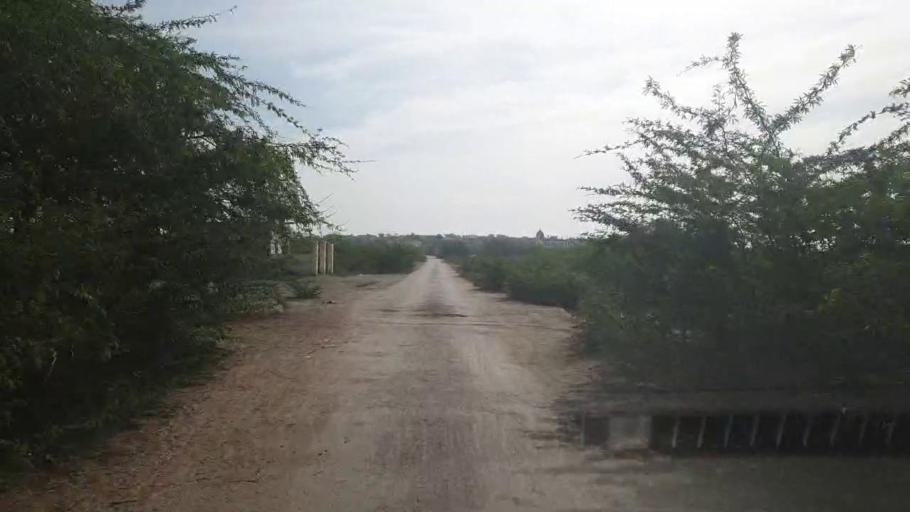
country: PK
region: Sindh
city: Umarkot
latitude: 25.3017
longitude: 69.7158
